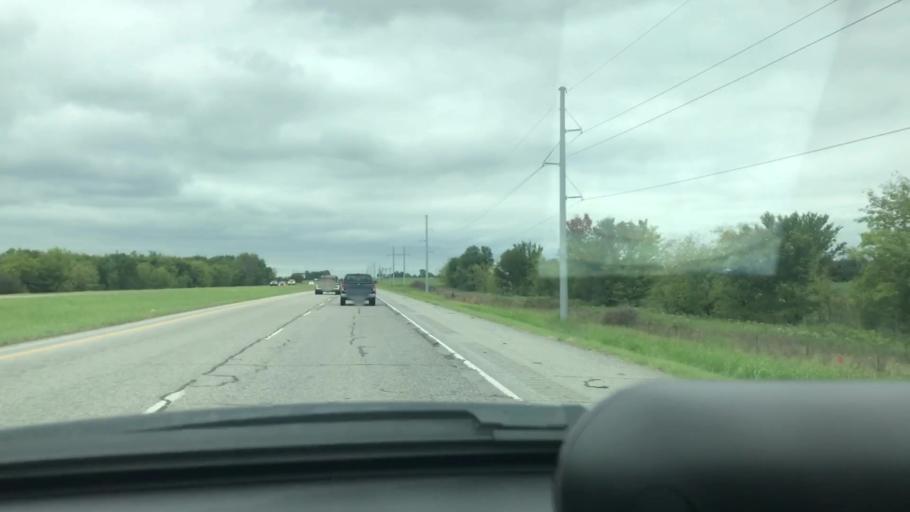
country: US
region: Oklahoma
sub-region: Wagoner County
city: Wagoner
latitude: 36.0030
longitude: -95.3686
